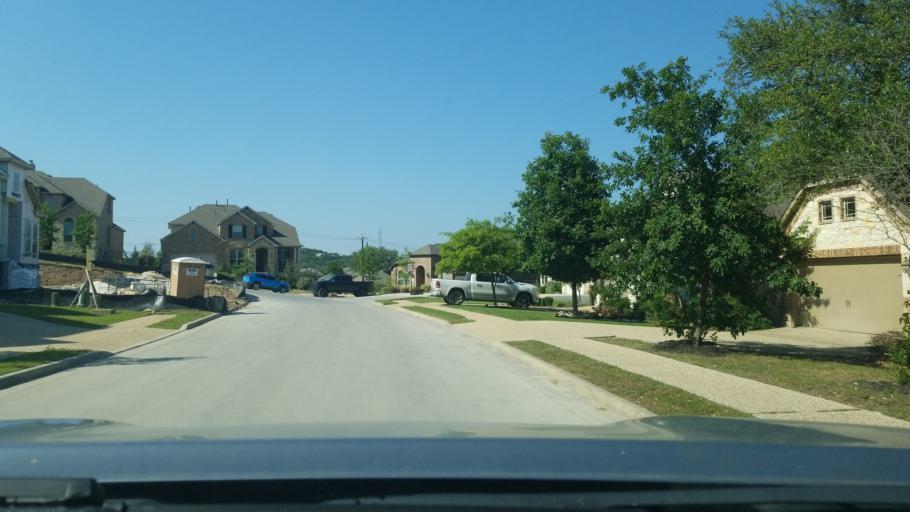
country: US
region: Texas
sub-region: Comal County
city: Bulverde
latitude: 29.7713
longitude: -98.4211
